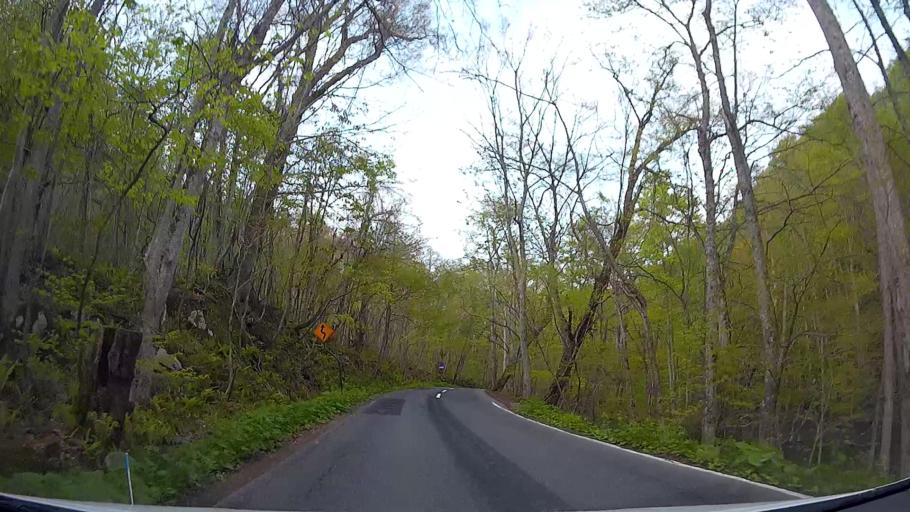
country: JP
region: Aomori
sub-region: Aomori Shi
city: Furudate
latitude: 40.5222
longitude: 140.9729
